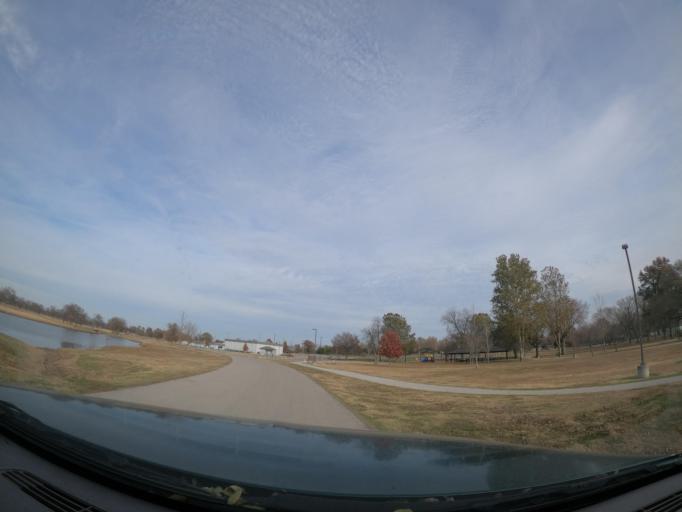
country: US
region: Oklahoma
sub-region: Tulsa County
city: Turley
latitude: 36.2439
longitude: -95.9561
